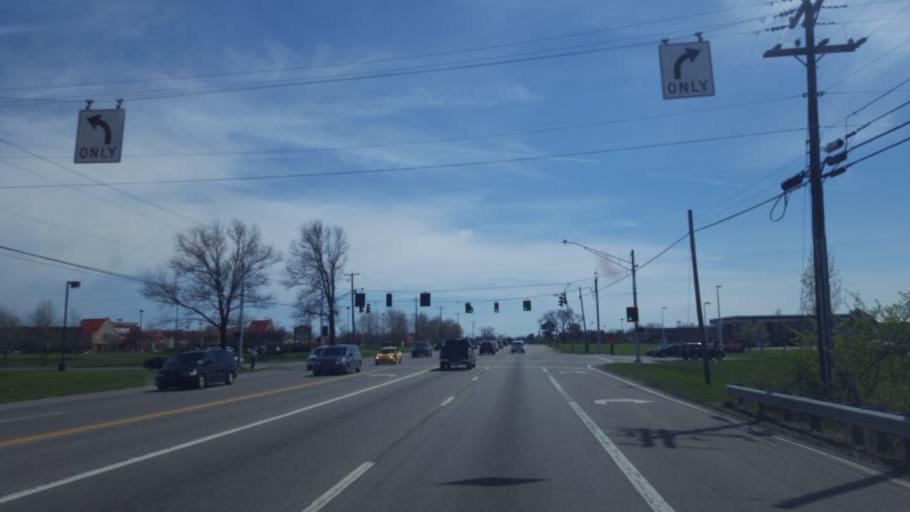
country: US
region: Ohio
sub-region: Delaware County
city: Lewis Center
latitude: 40.1624
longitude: -83.0195
